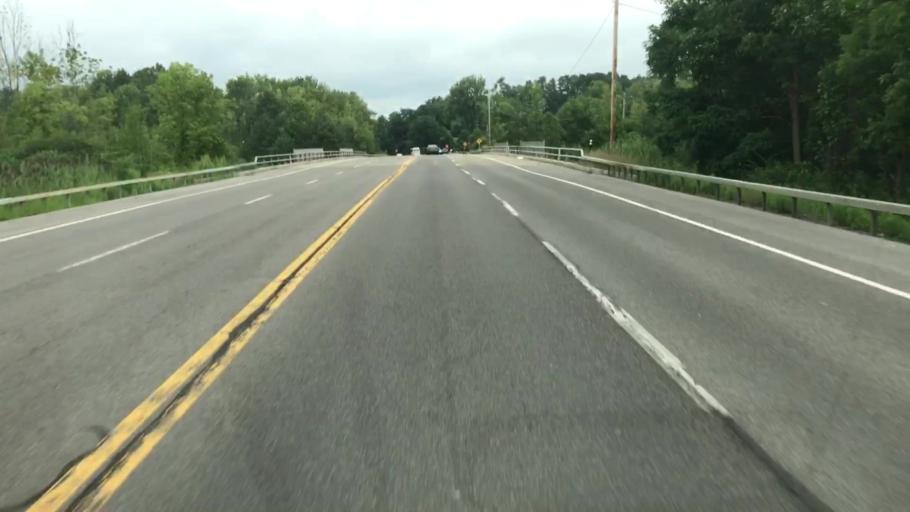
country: US
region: New York
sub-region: Onondaga County
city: Liverpool
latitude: 43.1720
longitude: -76.2092
